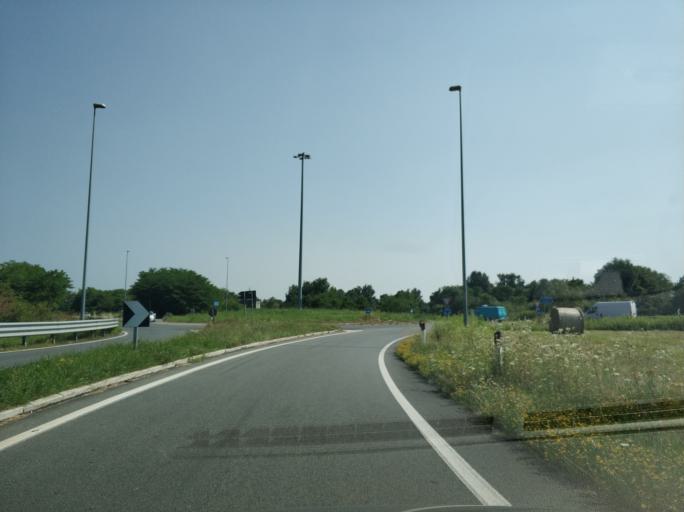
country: IT
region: Piedmont
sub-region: Provincia di Torino
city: Oglianico
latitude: 45.3527
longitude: 7.6991
